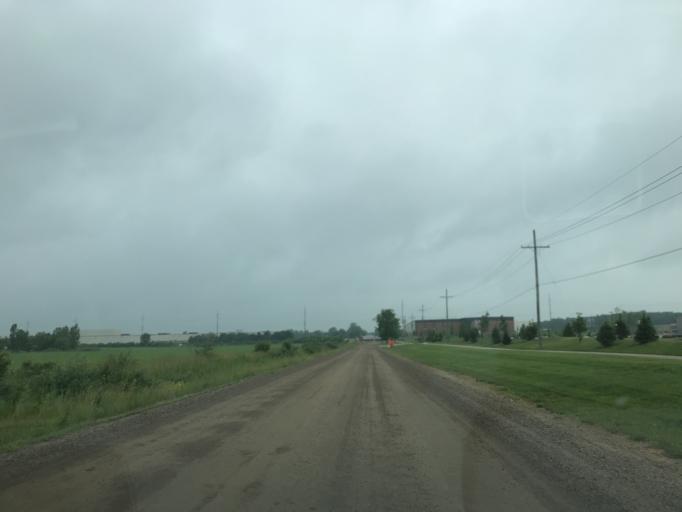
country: US
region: Michigan
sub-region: Oakland County
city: Wixom
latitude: 42.5041
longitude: -83.5955
